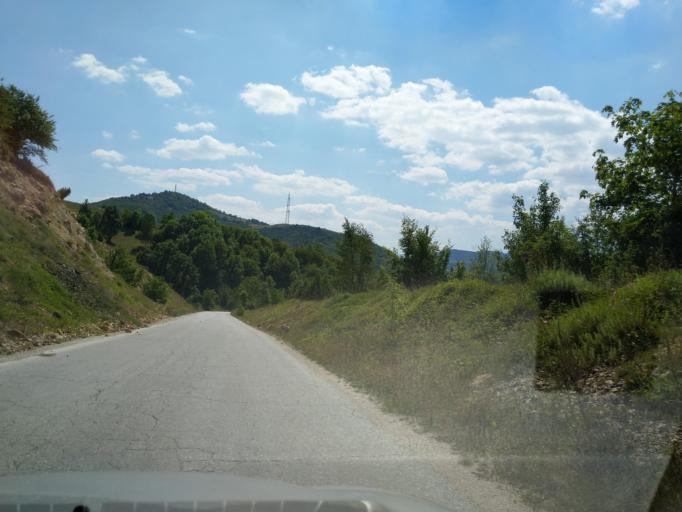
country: RS
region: Central Serbia
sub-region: Zlatiborski Okrug
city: Nova Varos
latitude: 43.4222
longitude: 19.9367
